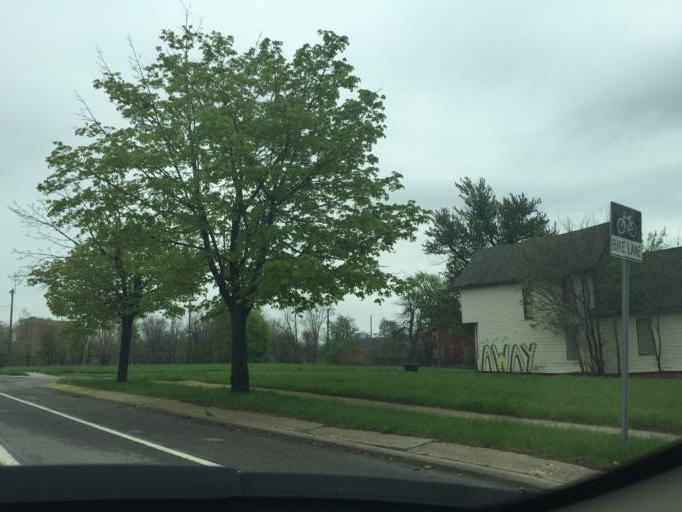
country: US
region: Michigan
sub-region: Wayne County
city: Detroit
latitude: 42.3386
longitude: -83.0826
